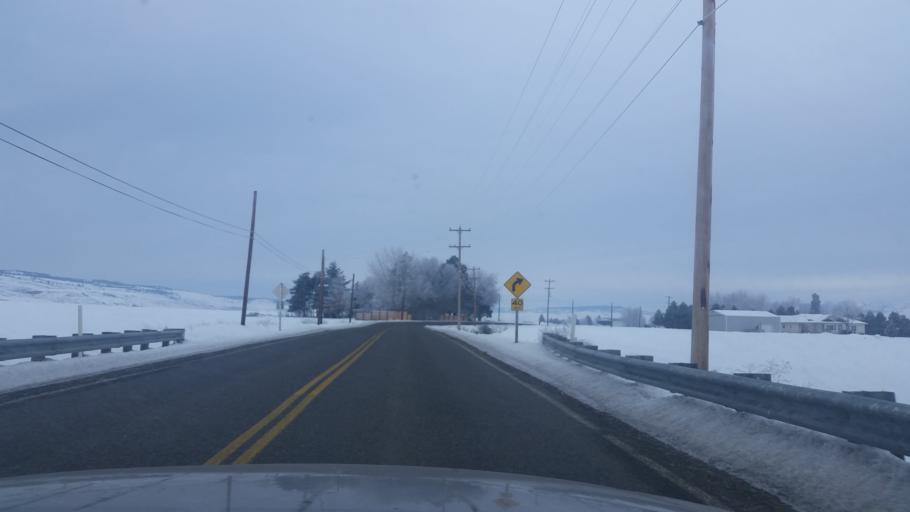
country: US
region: Washington
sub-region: Kittitas County
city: Ellensburg
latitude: 47.0308
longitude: -120.6540
